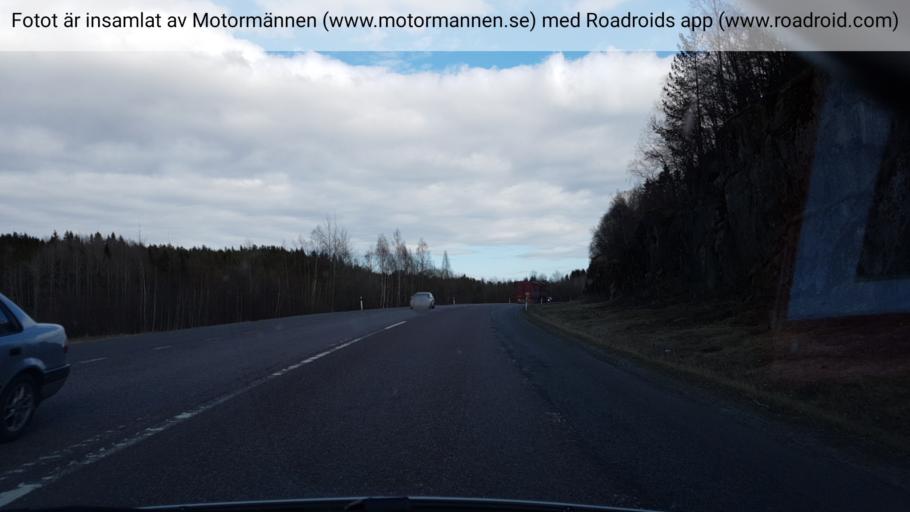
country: SE
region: Vaesternorrland
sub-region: Kramfors Kommun
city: Kramfors
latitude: 62.8996
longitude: 17.8418
